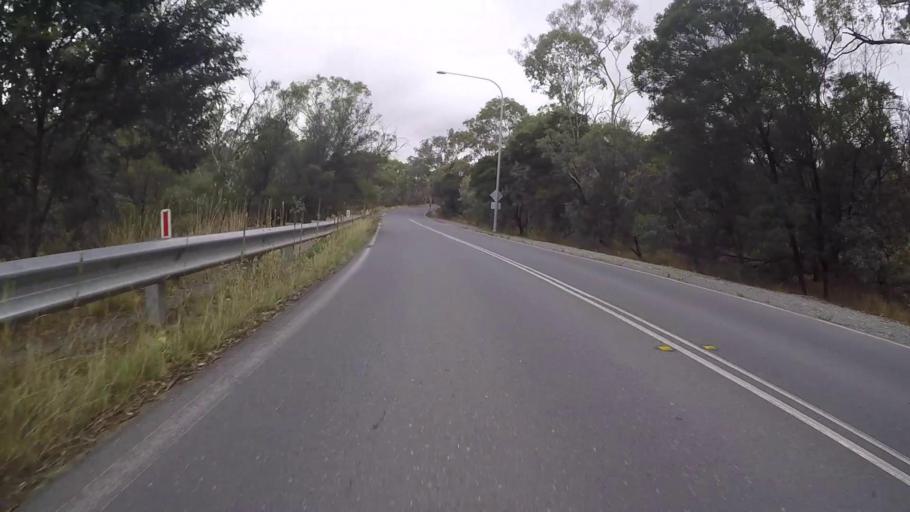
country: AU
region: Australian Capital Territory
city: Canberra
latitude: -35.2958
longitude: 149.1562
